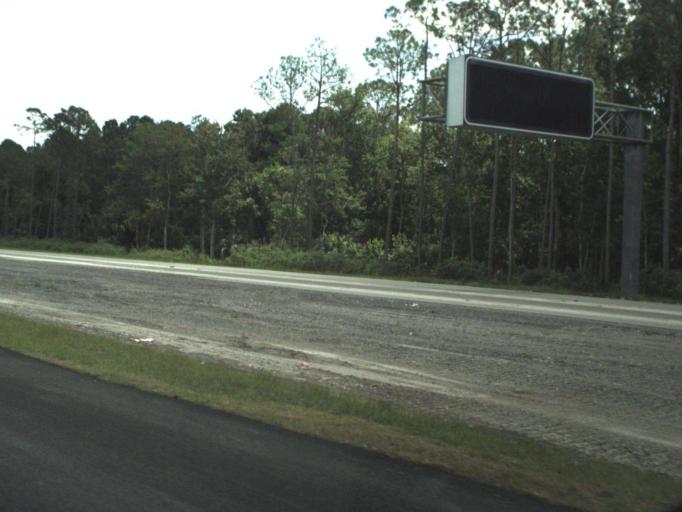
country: US
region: Florida
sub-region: Volusia County
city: South Daytona
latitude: 29.1455
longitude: -81.0992
